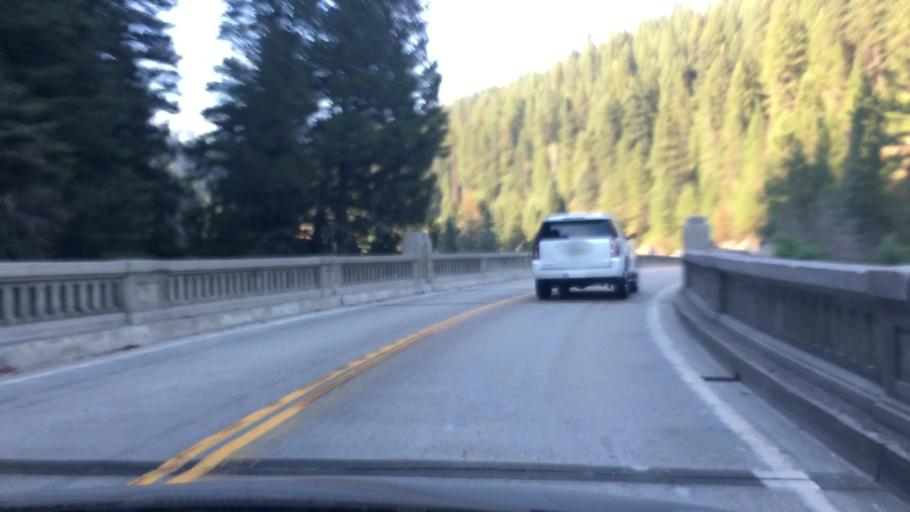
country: US
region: Idaho
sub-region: Valley County
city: Cascade
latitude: 44.3248
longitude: -116.0601
